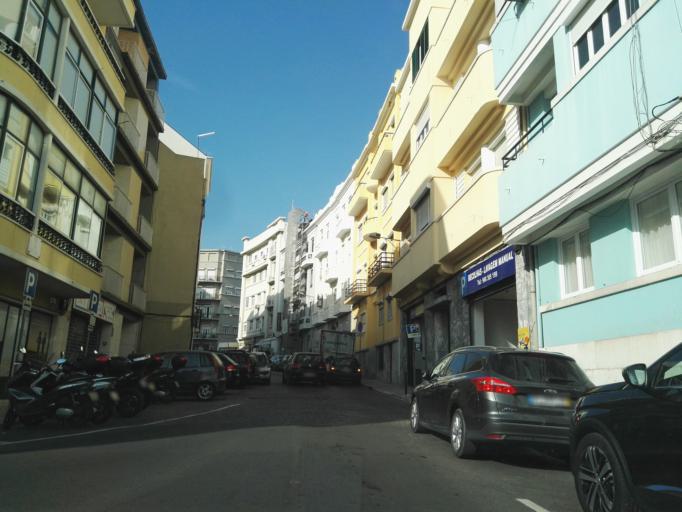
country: PT
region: Lisbon
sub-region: Lisbon
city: Lisbon
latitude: 38.7228
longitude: -9.1543
